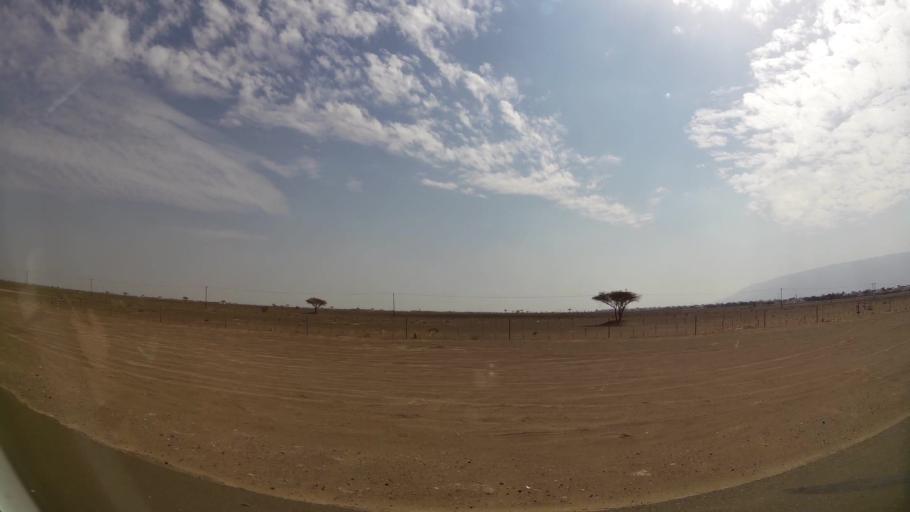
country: AE
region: Abu Dhabi
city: Al Ain
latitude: 24.0927
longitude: 55.8794
